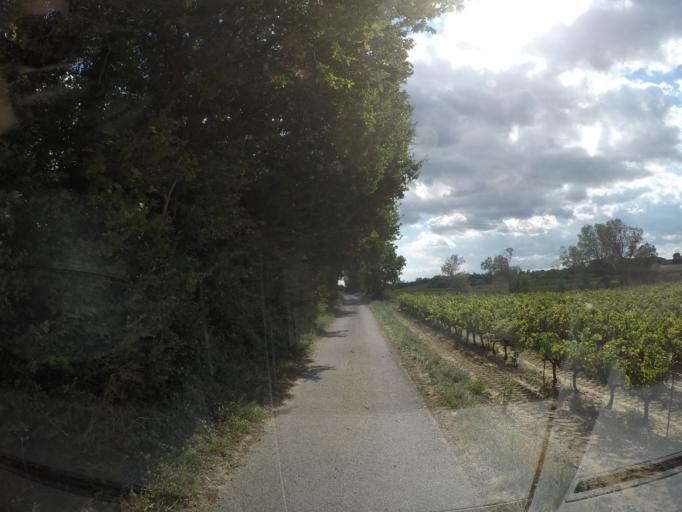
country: FR
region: Rhone-Alpes
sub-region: Departement de la Drome
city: Suze-la-Rousse
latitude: 44.2977
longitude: 4.8126
